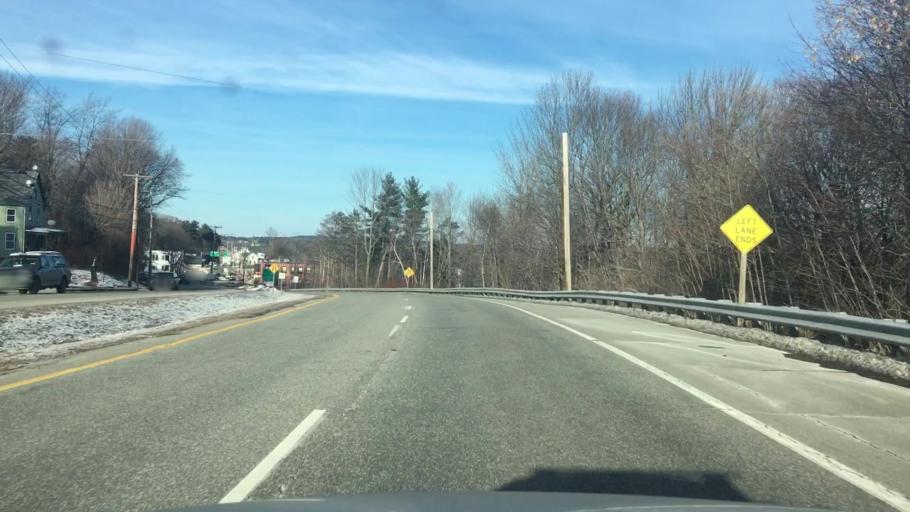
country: US
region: Maine
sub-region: Androscoggin County
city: Auburn
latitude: 44.0842
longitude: -70.2323
